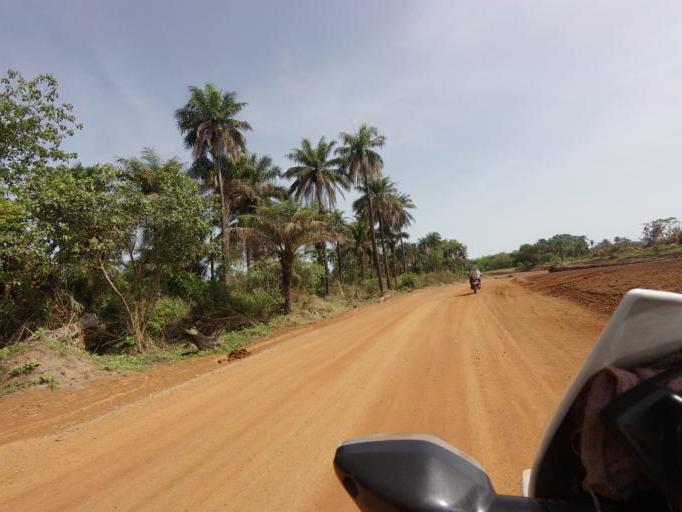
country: SL
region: Northern Province
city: Makeni
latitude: 9.0742
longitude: -12.1810
